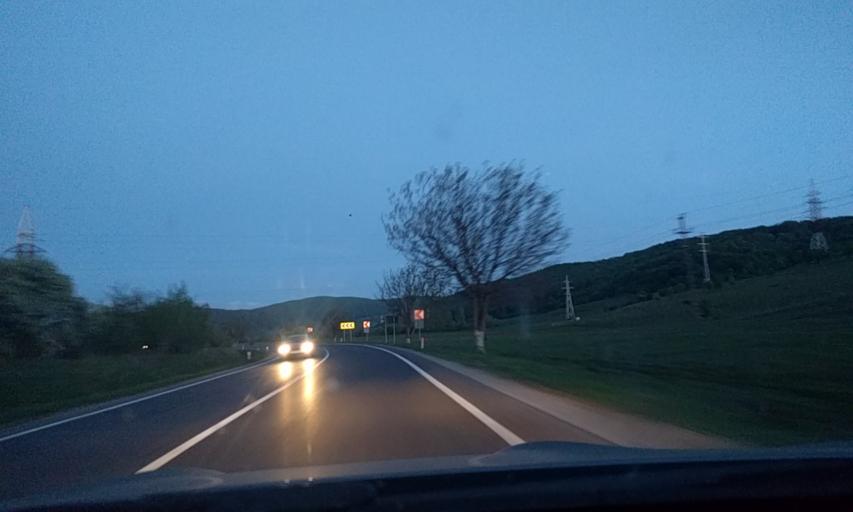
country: RO
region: Mures
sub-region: Comuna Vanatori
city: Vanatori
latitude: 46.2392
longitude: 24.9614
